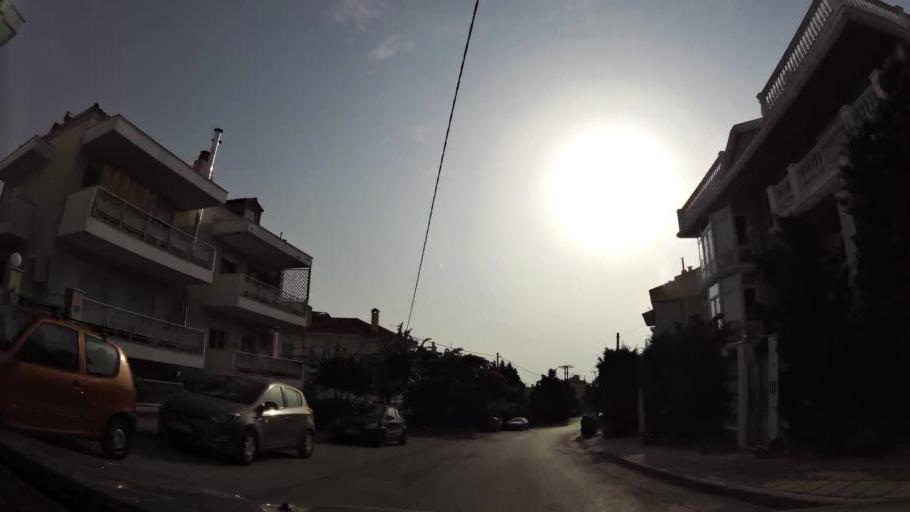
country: GR
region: Central Macedonia
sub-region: Nomos Thessalonikis
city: Oraiokastro
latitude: 40.7205
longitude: 22.9166
